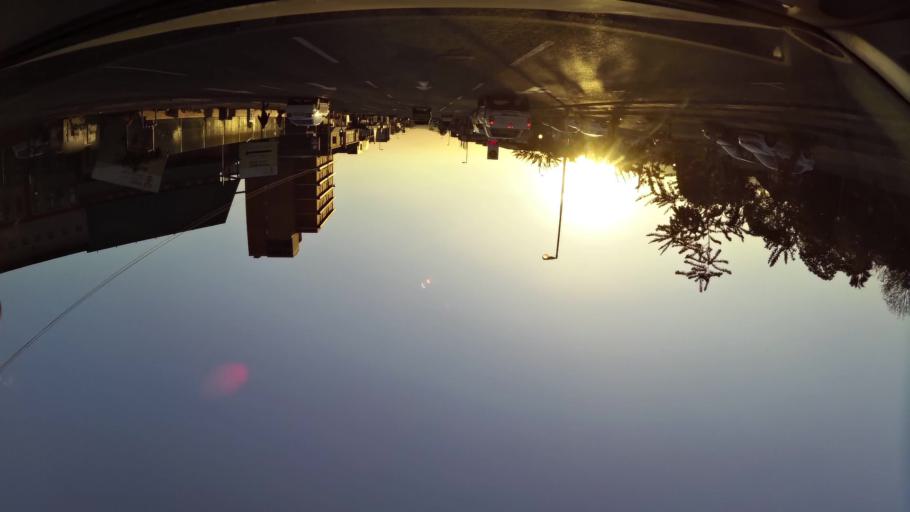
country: ZA
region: North-West
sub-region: Bojanala Platinum District Municipality
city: Rustenburg
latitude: -25.6722
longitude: 27.2426
